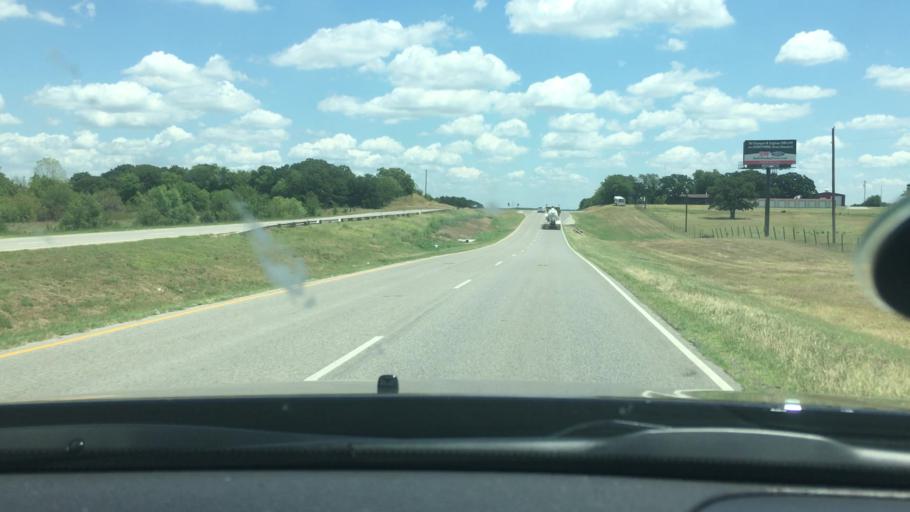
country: US
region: Oklahoma
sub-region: Carter County
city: Wilson
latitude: 34.1728
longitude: -97.3904
